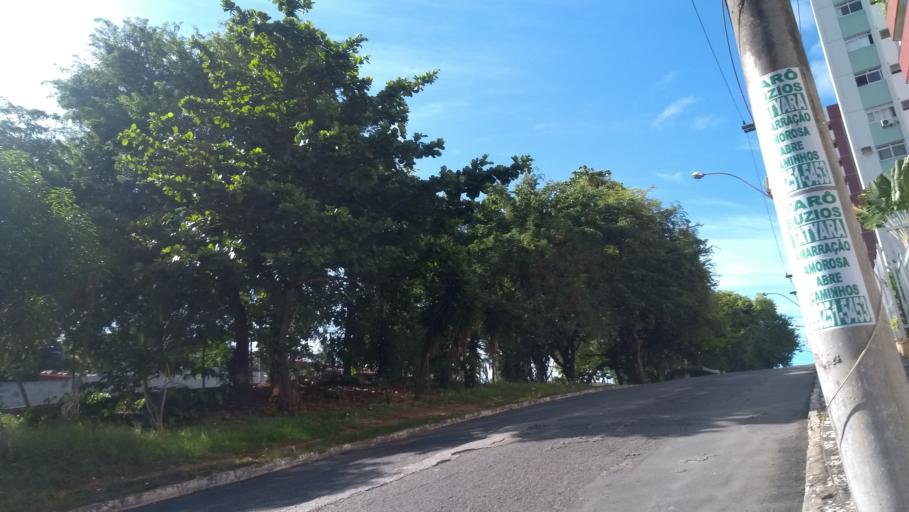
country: BR
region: Bahia
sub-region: Salvador
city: Salvador
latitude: -12.9972
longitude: -38.4596
